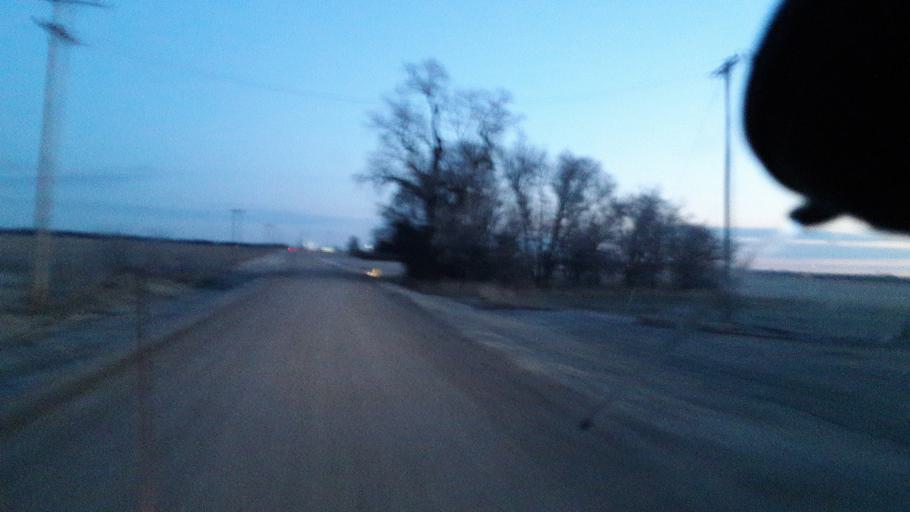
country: US
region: Kansas
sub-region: Reno County
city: South Hutchinson
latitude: 38.0055
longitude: -97.9768
